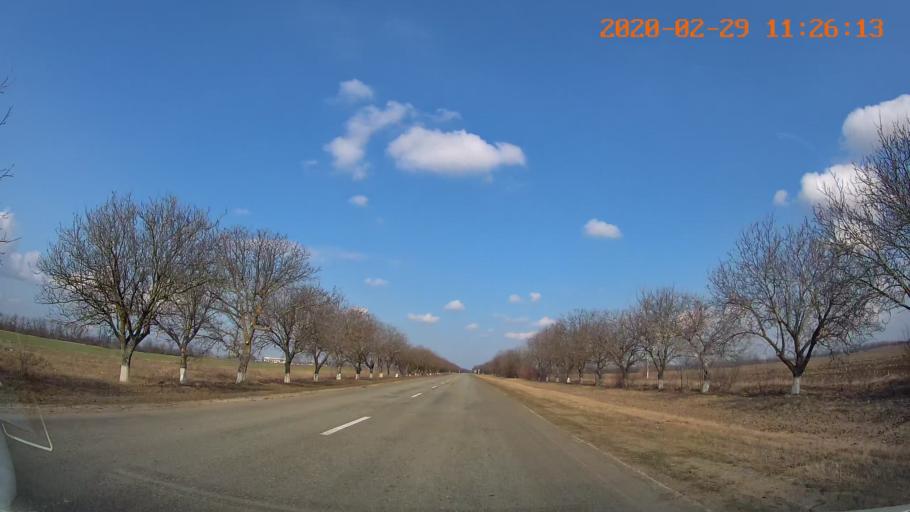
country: MD
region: Telenesti
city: Cocieri
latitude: 47.4500
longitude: 29.1470
